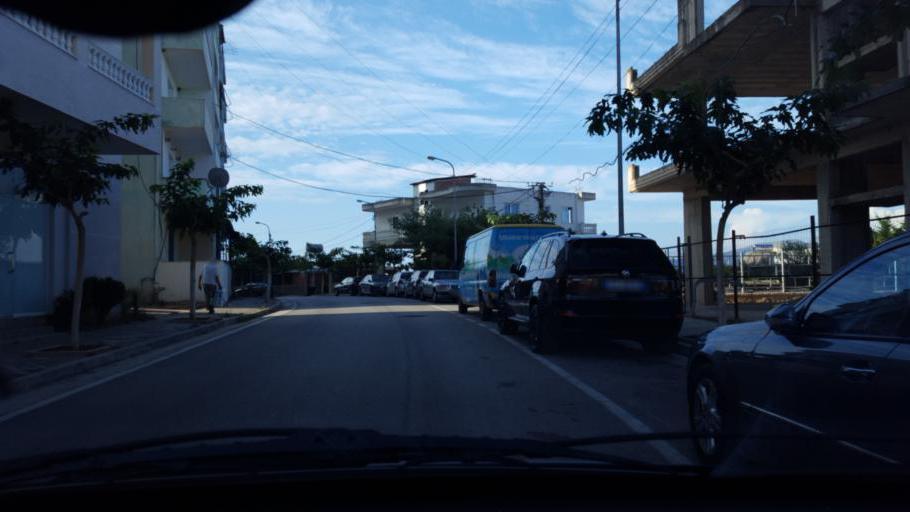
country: AL
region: Vlore
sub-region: Rrethi i Sarandes
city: Sarande
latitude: 39.8737
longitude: 19.9913
